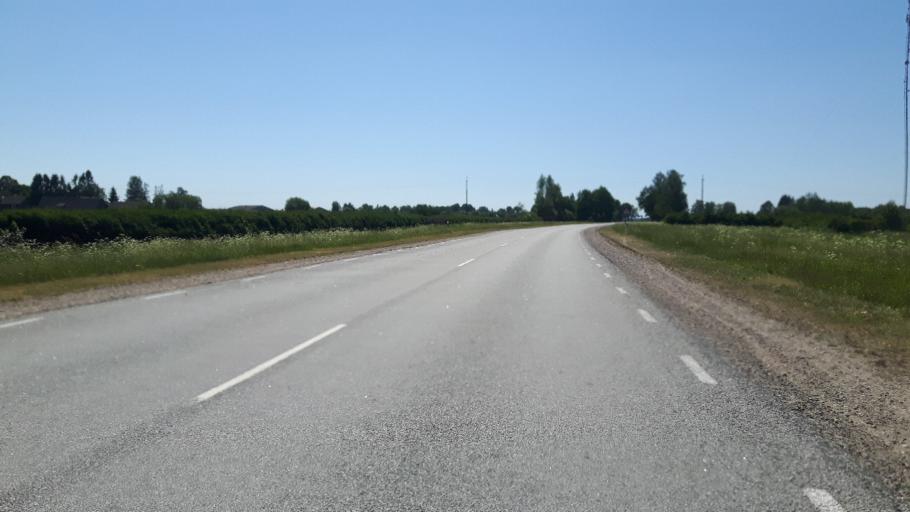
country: EE
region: Paernumaa
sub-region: Sindi linn
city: Sindi
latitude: 58.4503
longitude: 24.7737
